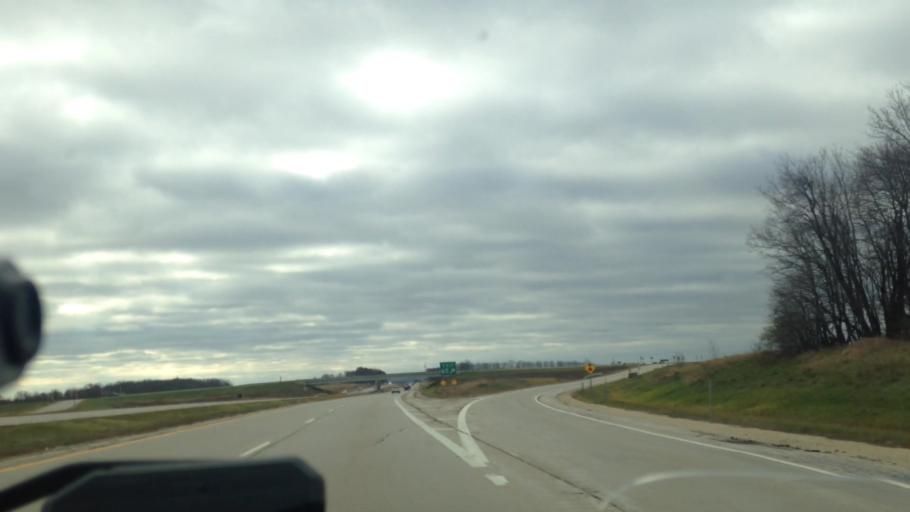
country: US
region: Wisconsin
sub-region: Washington County
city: Jackson
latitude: 43.3571
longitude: -88.1916
